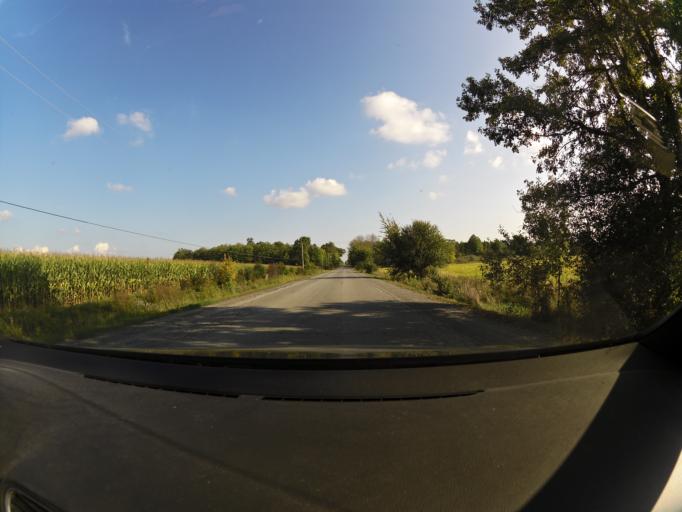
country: CA
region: Ontario
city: Arnprior
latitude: 45.4304
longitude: -76.2388
